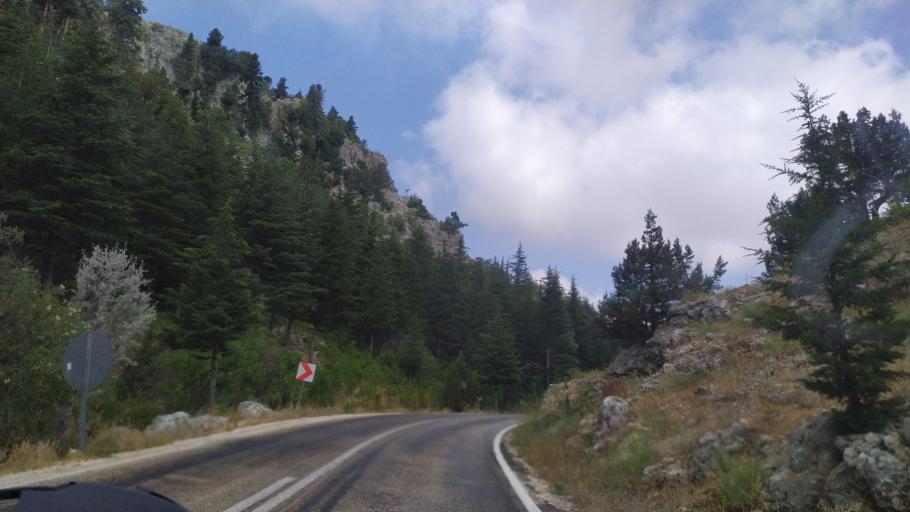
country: TR
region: Mersin
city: Kirobasi
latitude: 36.6096
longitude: 33.8818
